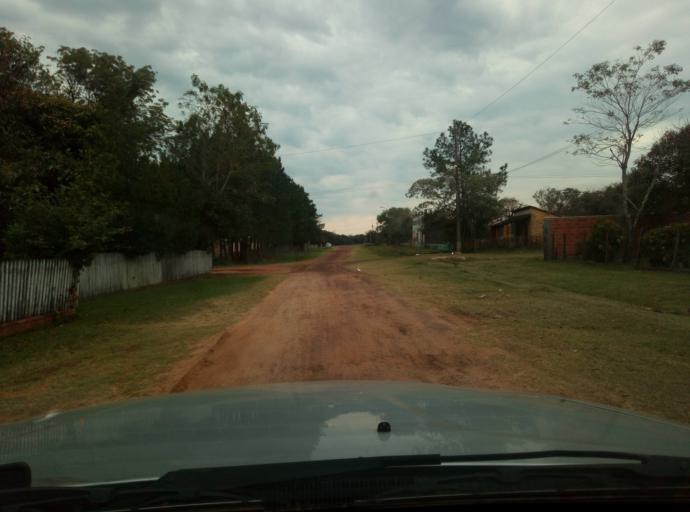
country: PY
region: Caaguazu
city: Carayao
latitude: -25.1530
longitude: -56.3337
